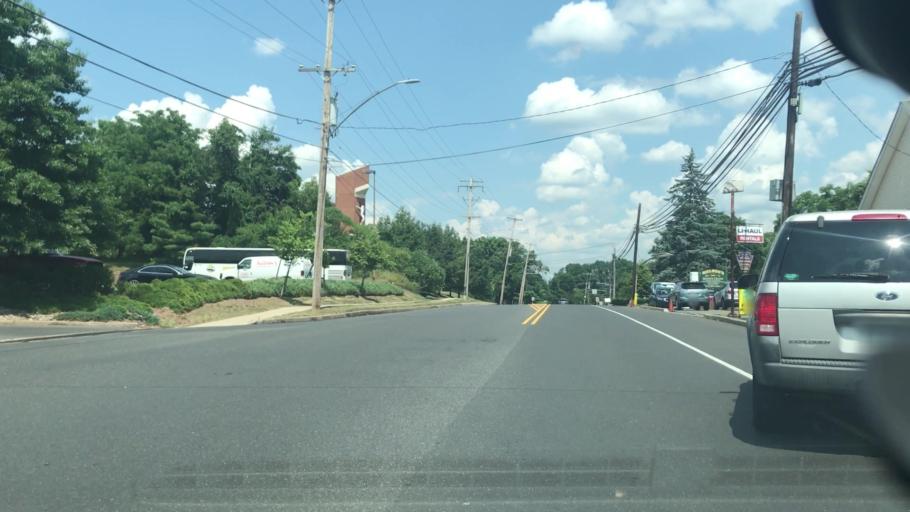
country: US
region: Pennsylvania
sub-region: Bucks County
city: New Hope
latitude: 40.3636
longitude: -74.9649
